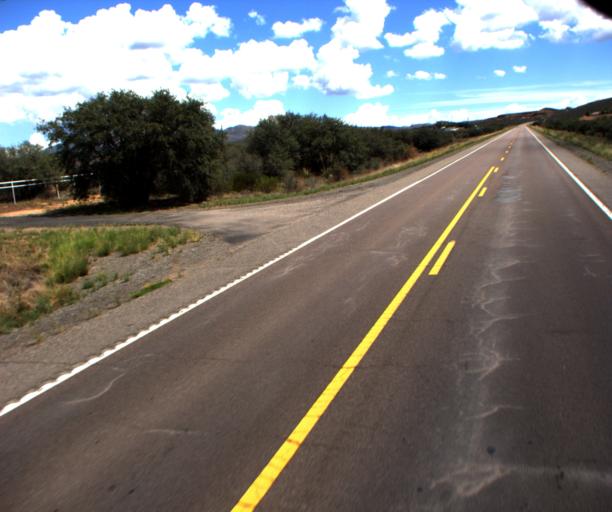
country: US
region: Arizona
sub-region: Yavapai County
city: Dewey-Humboldt
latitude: 34.5330
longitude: -112.2171
